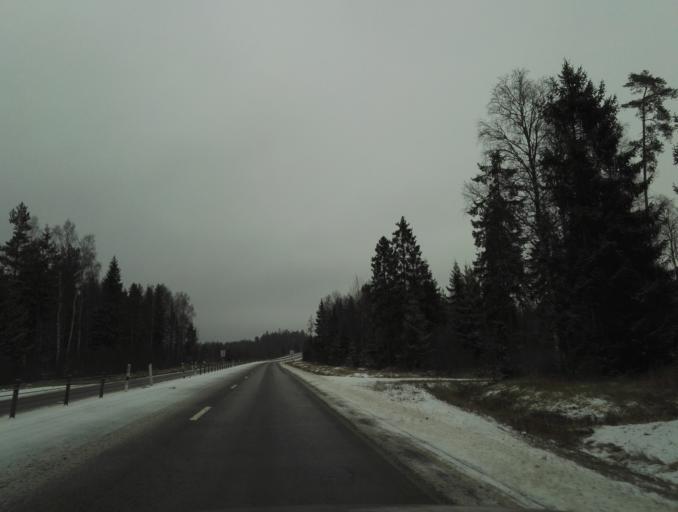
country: SE
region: Kronoberg
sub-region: Alvesta Kommun
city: Vislanda
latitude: 56.7431
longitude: 14.5092
